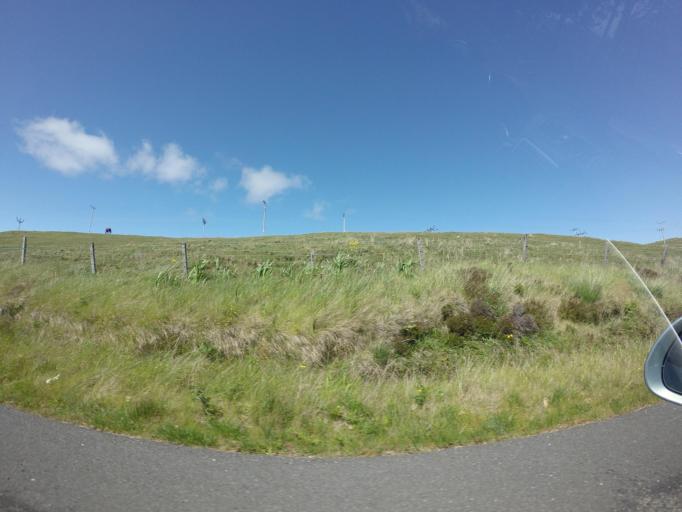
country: GB
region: Scotland
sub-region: Eilean Siar
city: Harris
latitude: 58.0896
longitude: -6.6223
